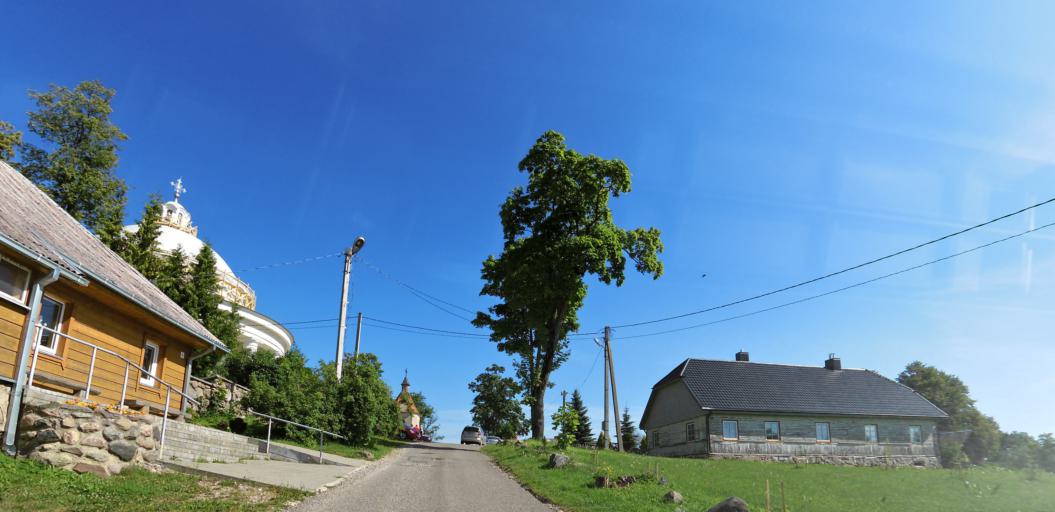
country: LT
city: Grigiskes
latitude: 54.7796
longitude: 25.0850
